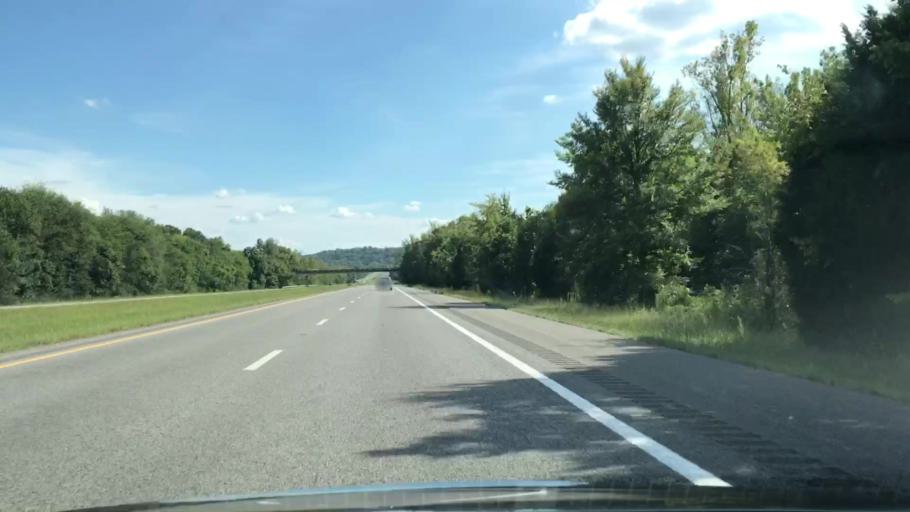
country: US
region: Alabama
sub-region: Limestone County
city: Ardmore
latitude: 35.1417
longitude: -86.8786
